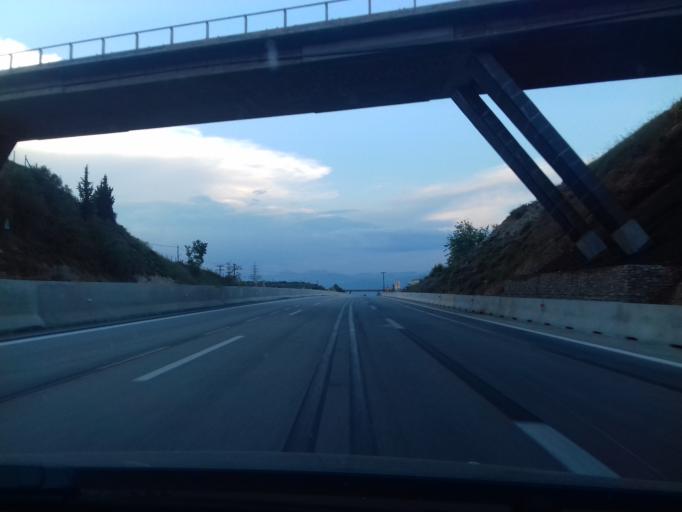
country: GR
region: West Greece
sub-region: Nomos Achaias
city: Aigio
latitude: 38.2426
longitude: 22.0742
